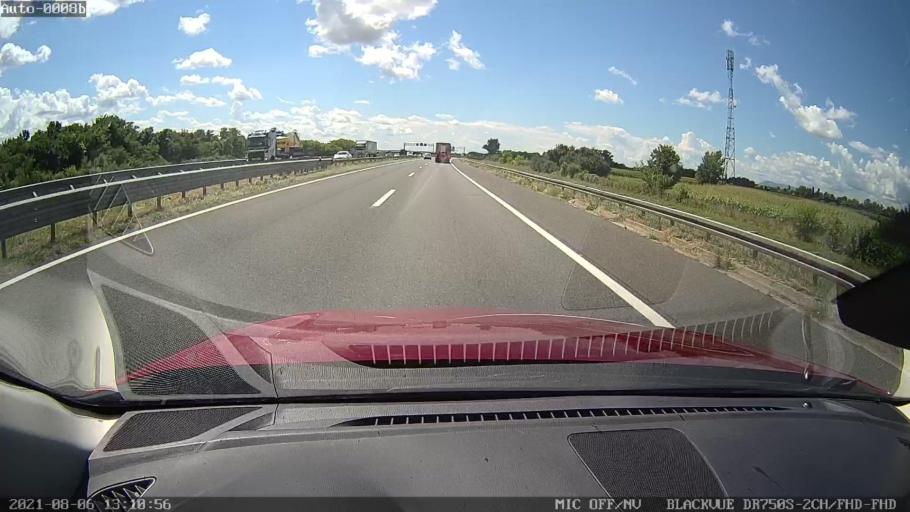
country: HR
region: Zagrebacka
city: Micevec
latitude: 45.7557
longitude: 16.0774
